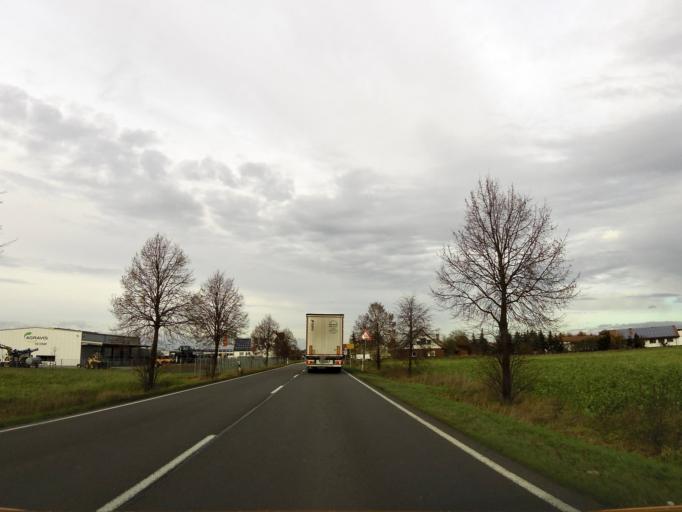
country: DE
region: Saxony-Anhalt
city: Pretzier
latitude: 52.7331
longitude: 11.2453
